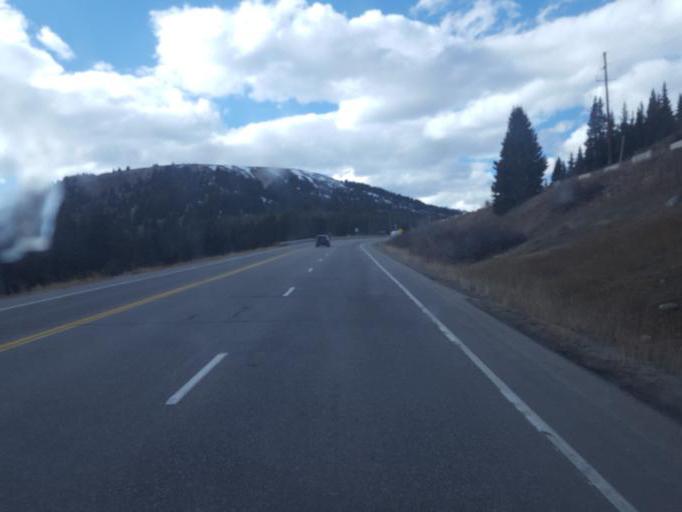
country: US
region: Colorado
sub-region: Lake County
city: Leadville
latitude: 39.3653
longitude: -106.1843
